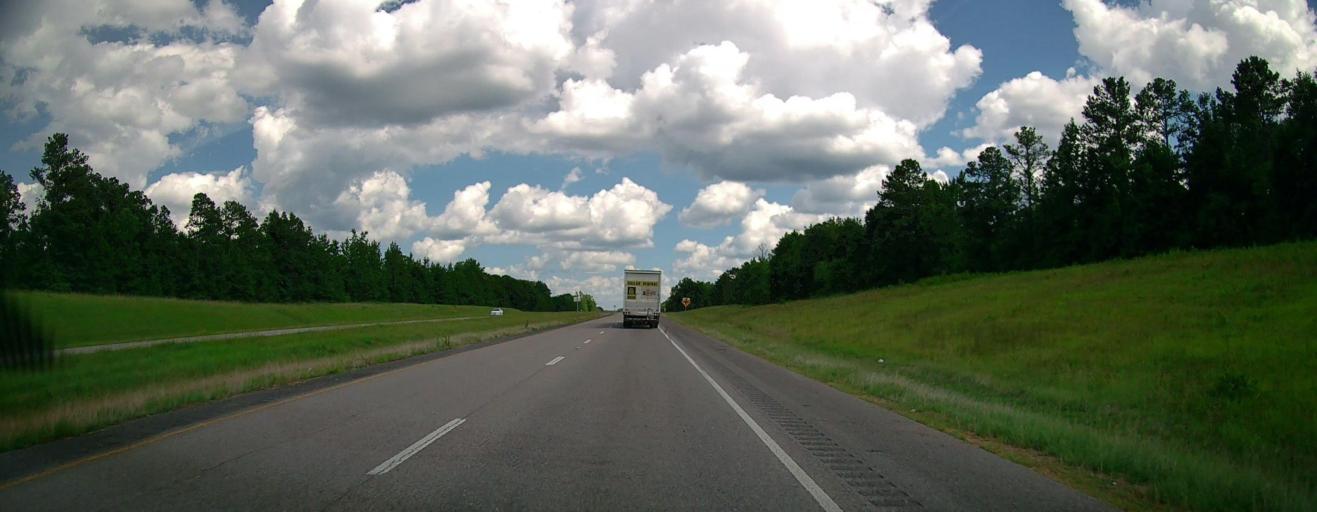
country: US
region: Mississippi
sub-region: Lowndes County
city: New Hope
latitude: 33.4884
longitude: -88.2705
